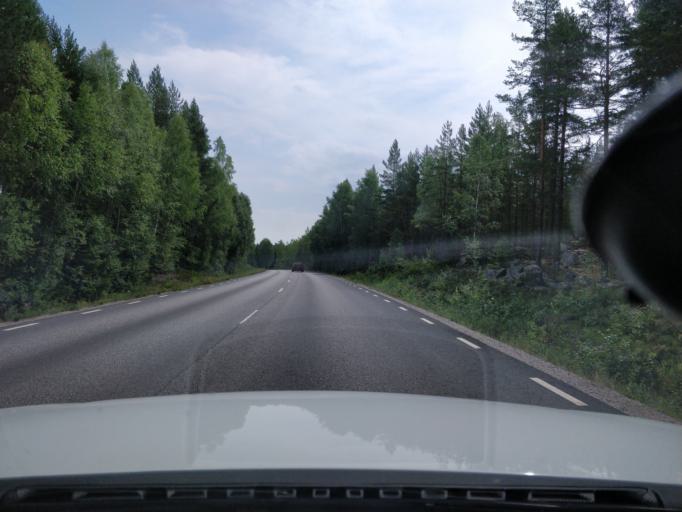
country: SE
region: Dalarna
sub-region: Ludvika Kommun
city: Ludvika
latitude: 60.2916
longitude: 15.2337
